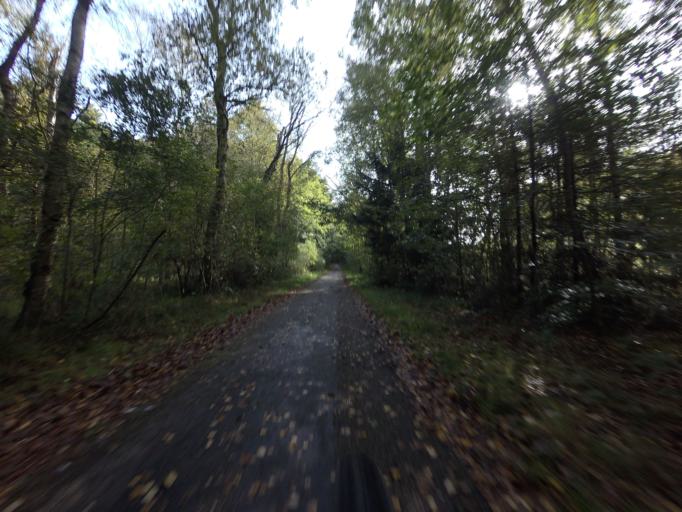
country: DK
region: Central Jutland
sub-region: Viborg Kommune
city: Viborg
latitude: 56.4243
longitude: 9.4400
